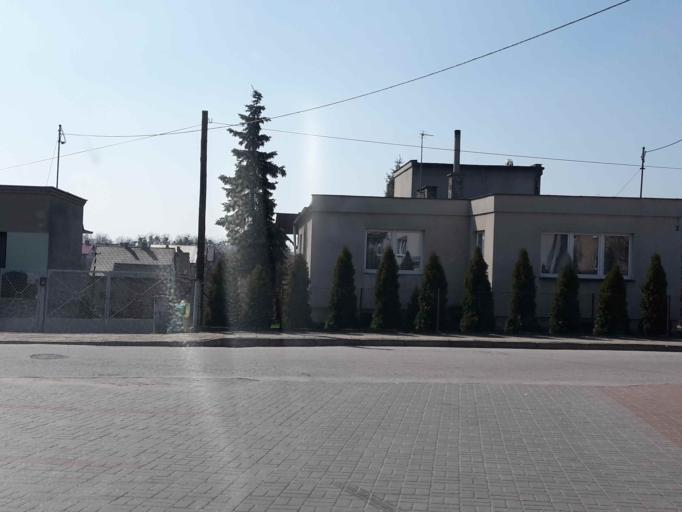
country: PL
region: Kujawsko-Pomorskie
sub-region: Powiat brodnicki
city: Brodnica
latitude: 53.2683
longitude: 19.4034
